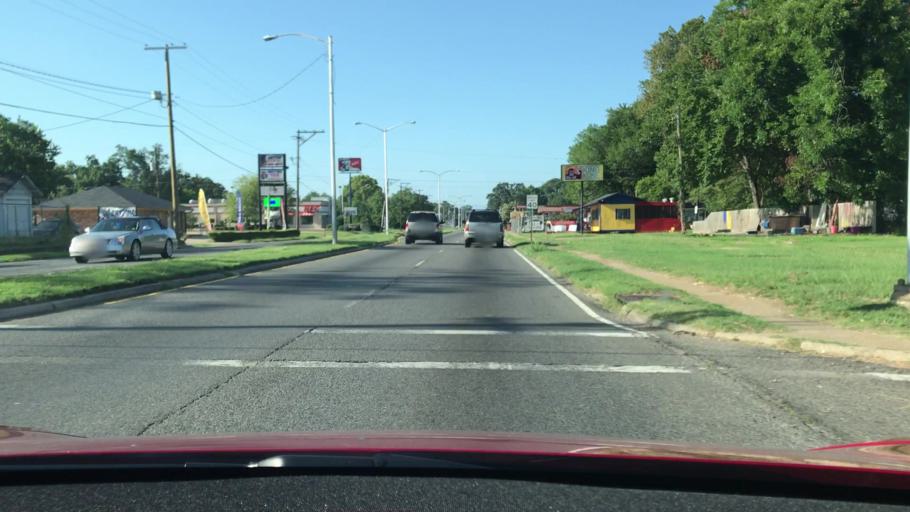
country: US
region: Louisiana
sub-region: Caddo Parish
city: Shreveport
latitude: 32.4764
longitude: -93.7801
